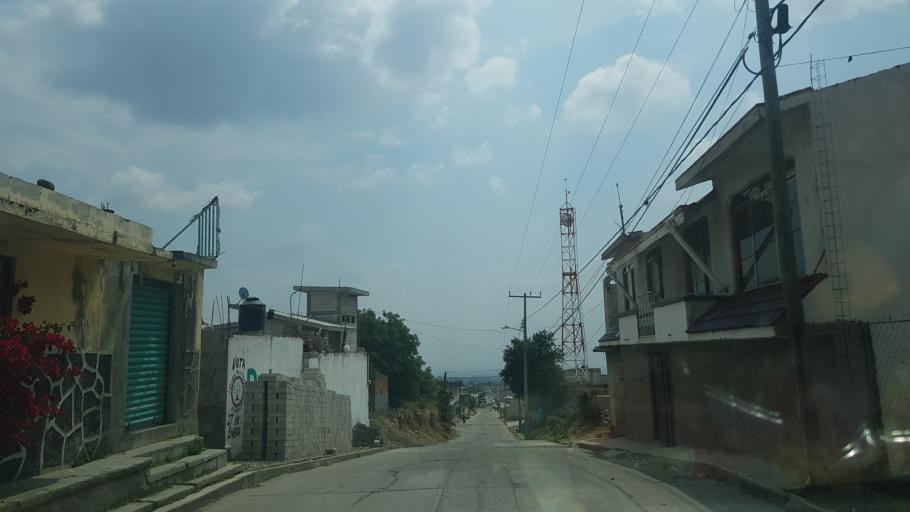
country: MX
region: Puebla
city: Domingo Arenas
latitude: 19.1358
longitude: -98.4952
